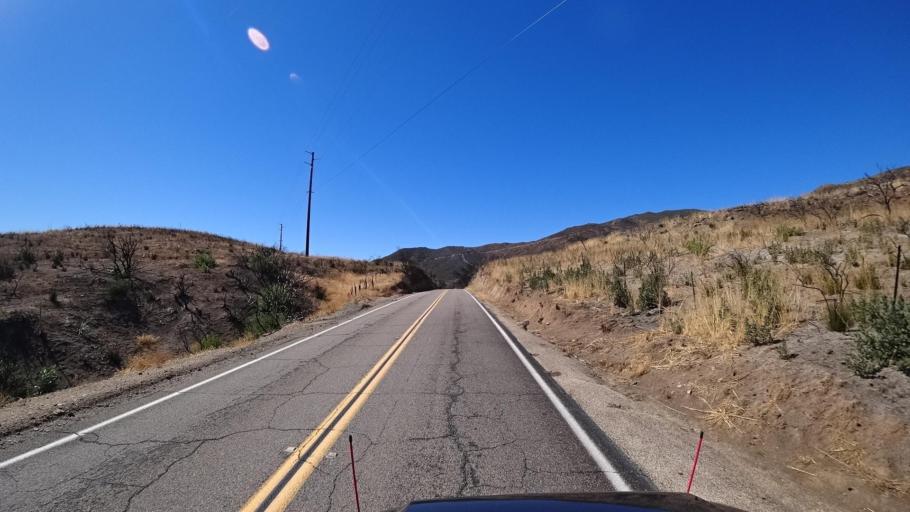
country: US
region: California
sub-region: San Diego County
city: Alpine
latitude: 32.7242
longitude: -116.7013
